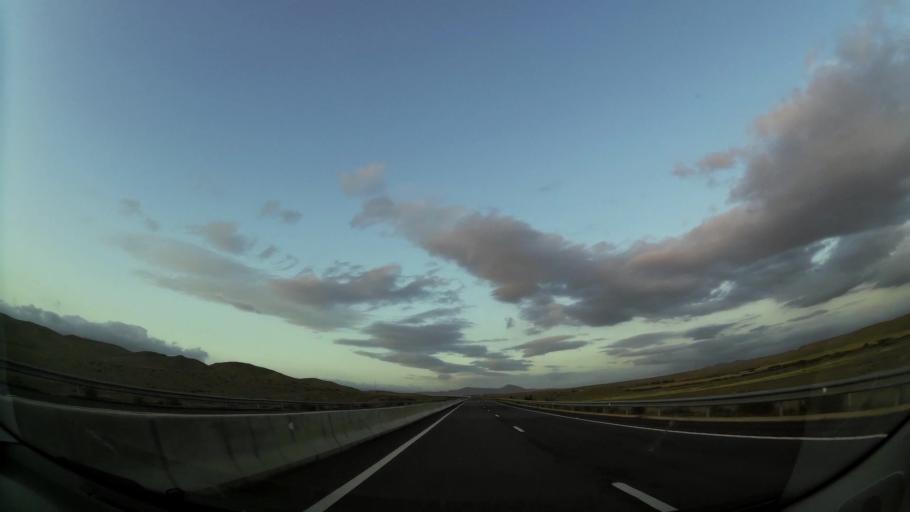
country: MA
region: Oriental
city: Taourirt
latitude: 34.5866
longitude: -2.7976
